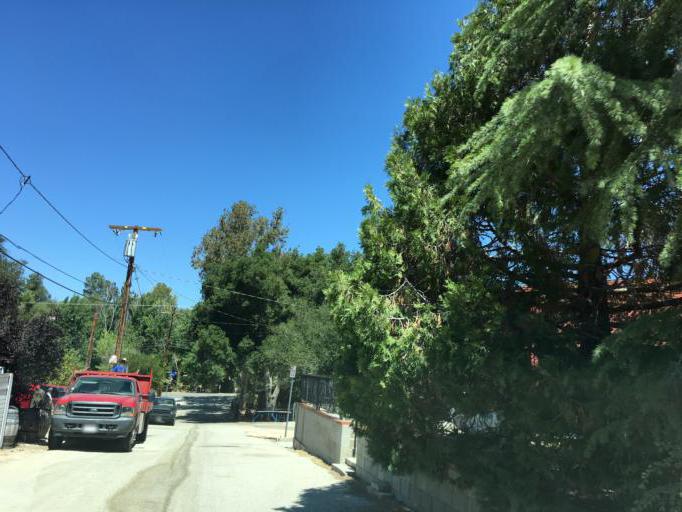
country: US
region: California
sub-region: Los Angeles County
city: Agua Dulce
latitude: 34.5092
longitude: -118.3622
